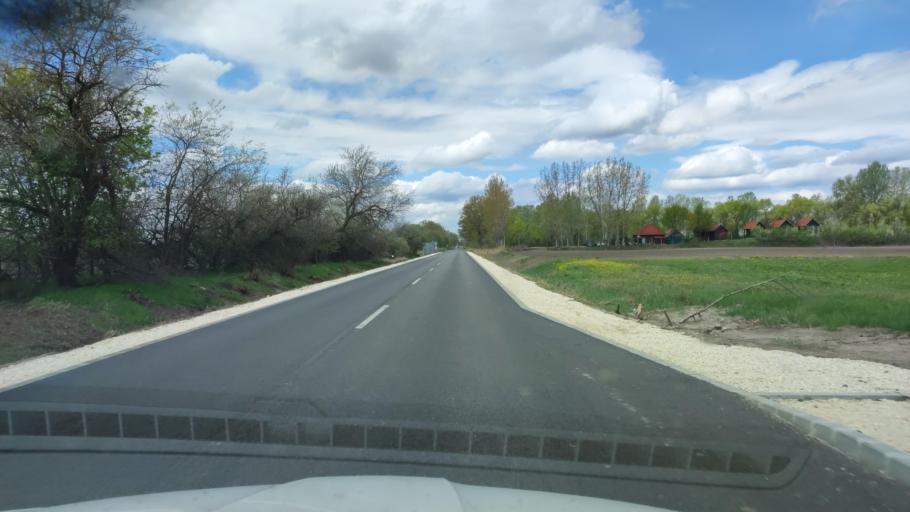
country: HU
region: Pest
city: Kocser
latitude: 46.9958
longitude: 19.9450
